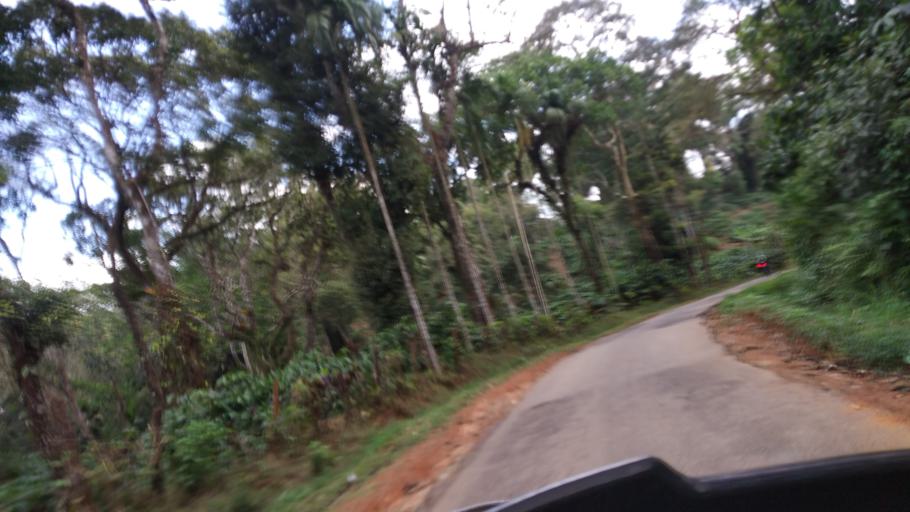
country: IN
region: Karnataka
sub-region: Kodagu
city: Ponnampet
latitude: 12.0371
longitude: 75.9098
